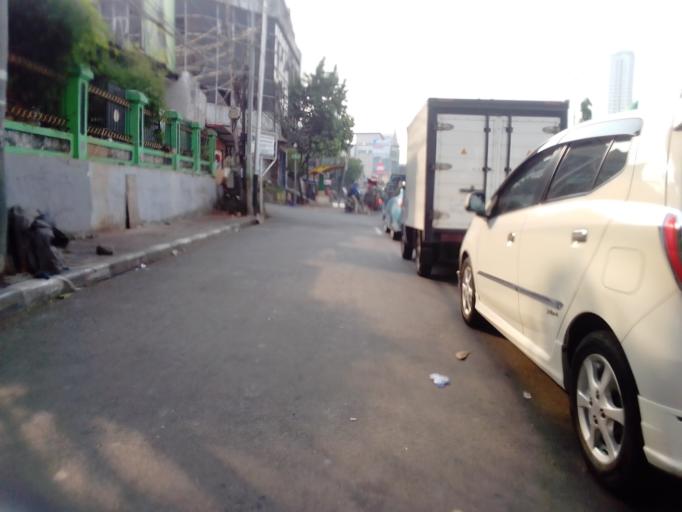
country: ID
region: Jakarta Raya
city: Jakarta
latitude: -6.1996
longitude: 106.8148
